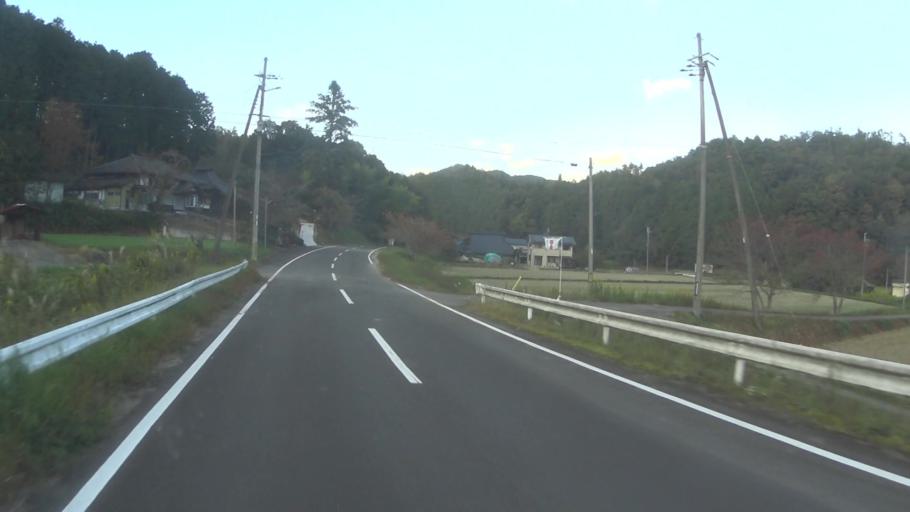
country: JP
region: Kyoto
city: Ayabe
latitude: 35.2814
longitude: 135.2378
